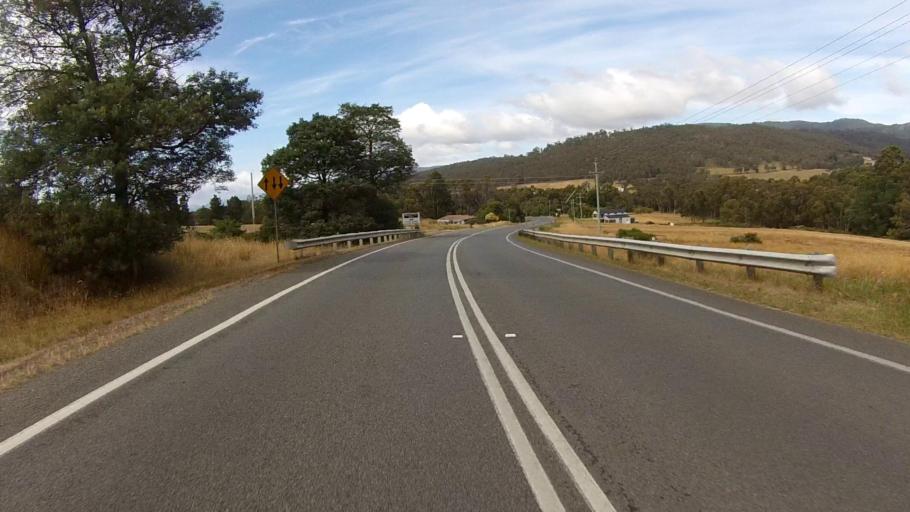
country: AU
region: Tasmania
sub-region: Kingborough
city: Kettering
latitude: -43.1155
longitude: 147.2450
